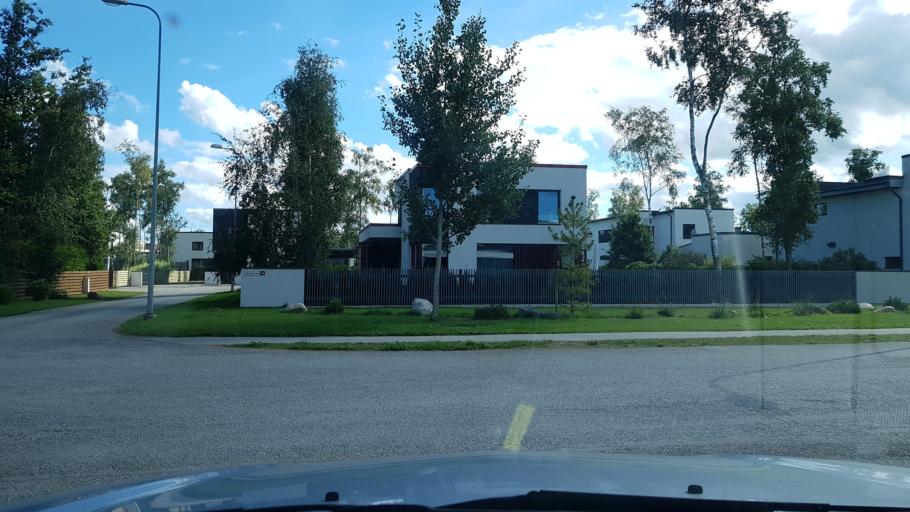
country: EE
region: Harju
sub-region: Tallinna linn
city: Tallinn
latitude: 59.4027
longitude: 24.7998
